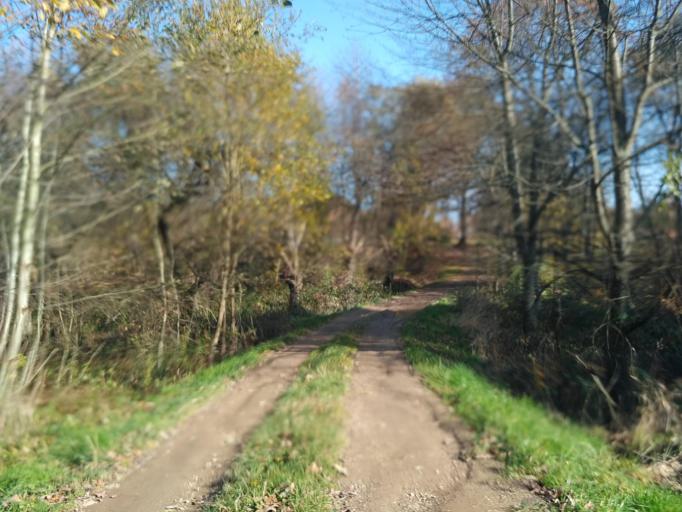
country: PL
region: Subcarpathian Voivodeship
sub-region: Powiat rzeszowski
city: Blazowa
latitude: 49.8602
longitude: 22.0851
